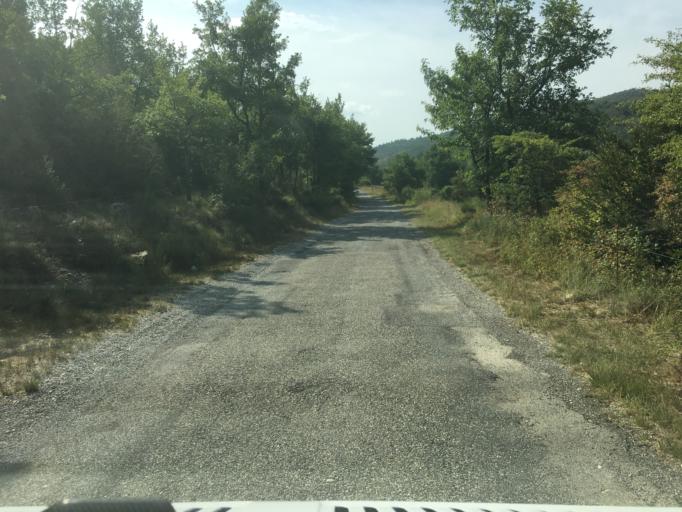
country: FR
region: Provence-Alpes-Cote d'Azur
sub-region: Departement des Alpes-de-Haute-Provence
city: Riez
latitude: 43.9208
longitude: 6.1915
